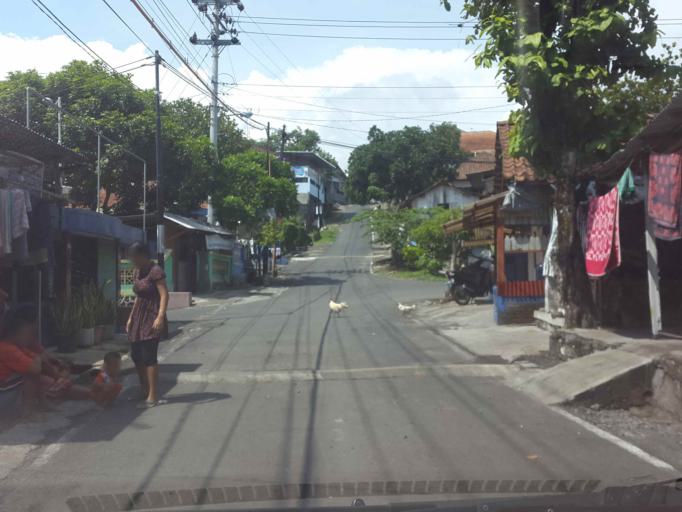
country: ID
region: Central Java
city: Salatiga
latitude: -7.3224
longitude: 110.5082
